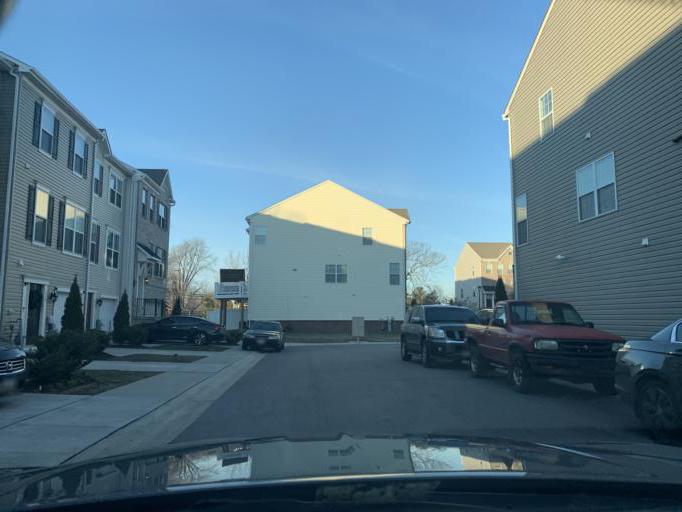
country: US
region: Maryland
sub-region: Anne Arundel County
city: Glen Burnie
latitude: 39.1518
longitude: -76.6342
